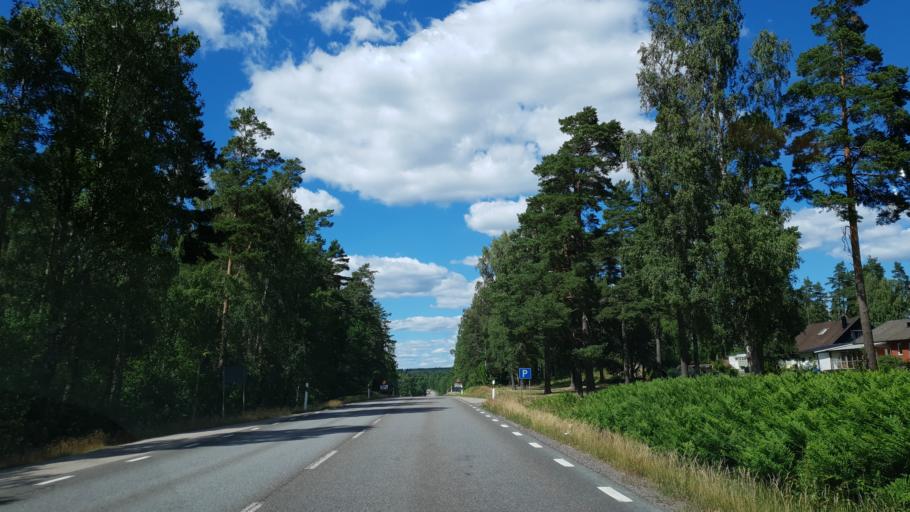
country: SE
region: Kronoberg
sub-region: Lessebo Kommun
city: Lessebo
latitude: 56.7632
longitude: 15.2649
